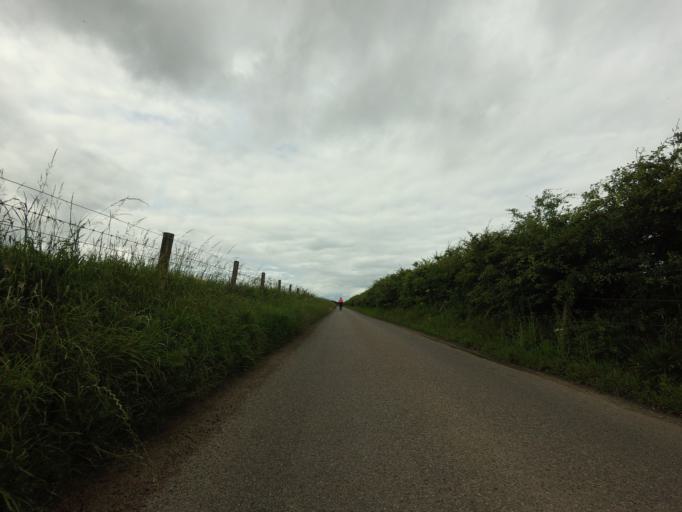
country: GB
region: Scotland
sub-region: Moray
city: Forres
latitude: 57.6220
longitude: -3.6669
